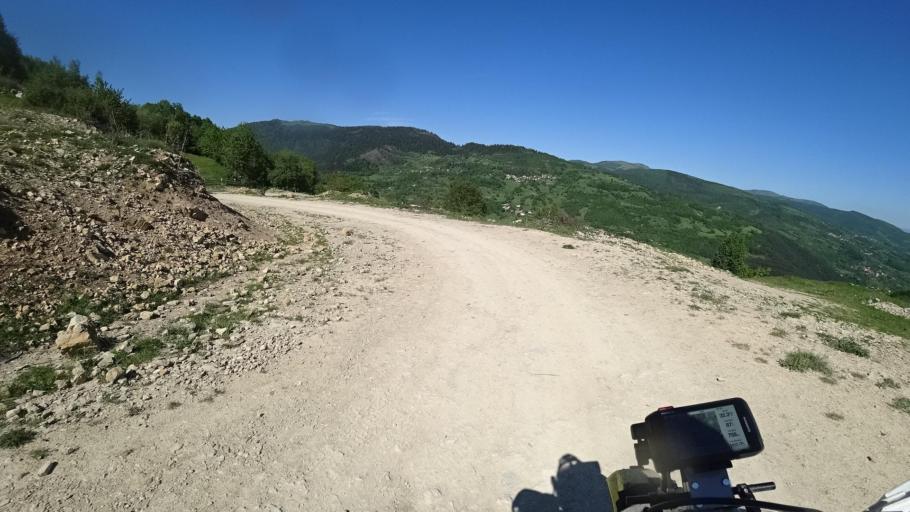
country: BA
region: Federation of Bosnia and Herzegovina
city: Travnik
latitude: 44.2783
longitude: 17.7097
